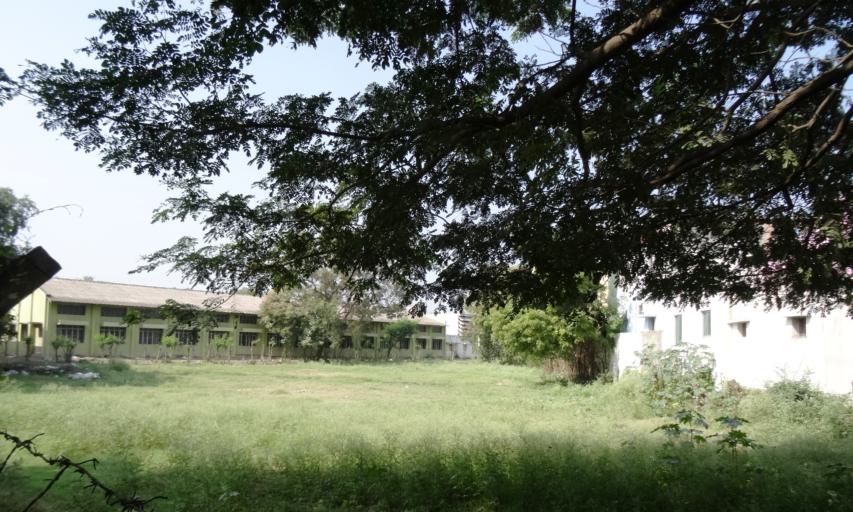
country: IN
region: Tamil Nadu
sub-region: Coimbatore
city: Perur
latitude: 10.9878
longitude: 76.9348
